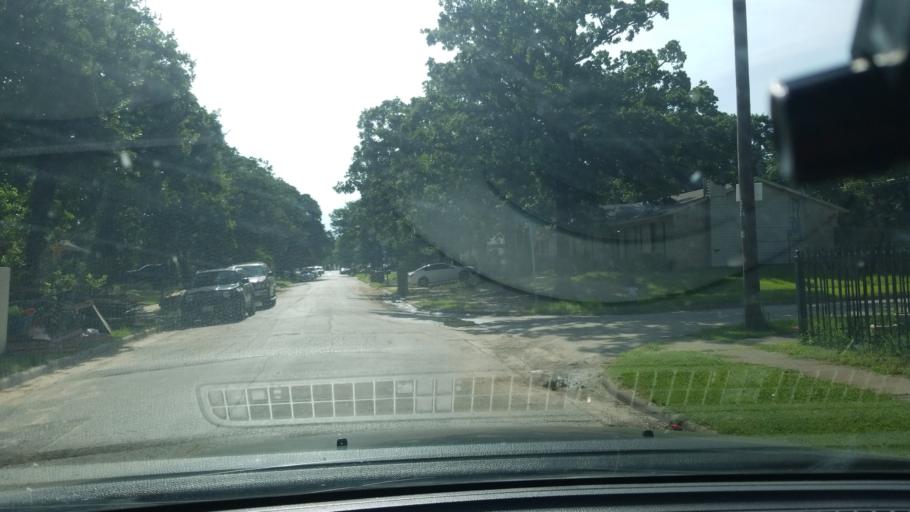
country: US
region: Texas
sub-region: Dallas County
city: Balch Springs
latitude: 32.7244
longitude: -96.6415
